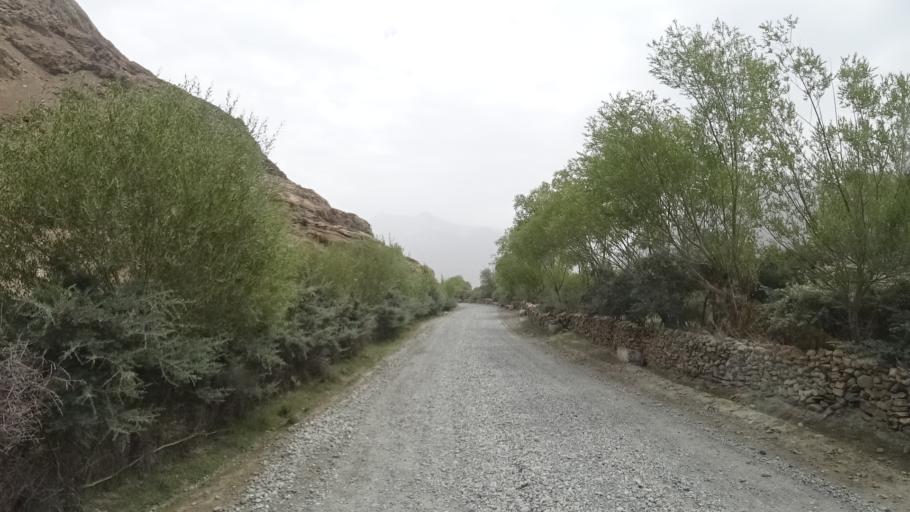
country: AF
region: Badakhshan
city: Khandud
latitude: 37.0219
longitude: 72.5982
